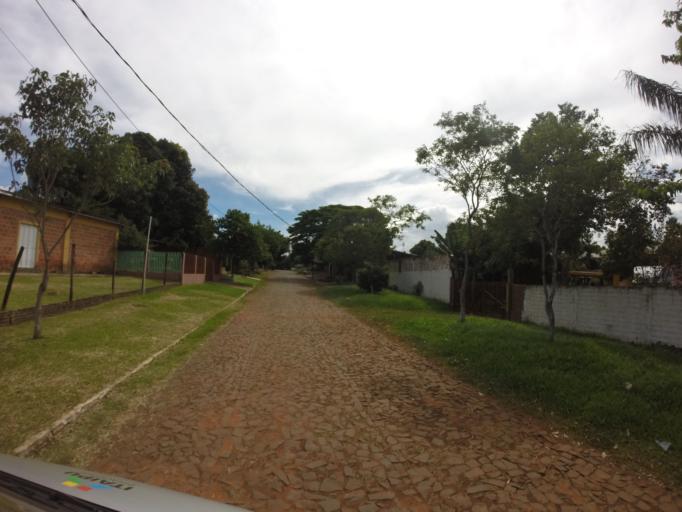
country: PY
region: Alto Parana
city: Ciudad del Este
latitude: -25.4338
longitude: -54.6393
